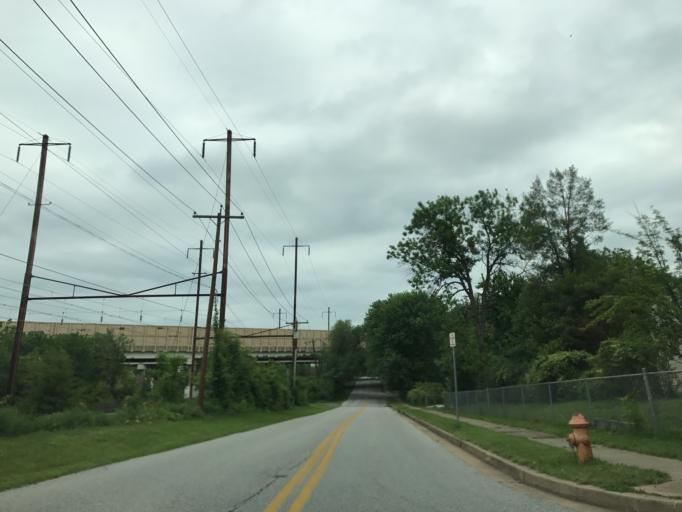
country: US
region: Maryland
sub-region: Baltimore County
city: Arbutus
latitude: 39.2418
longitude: -76.6908
